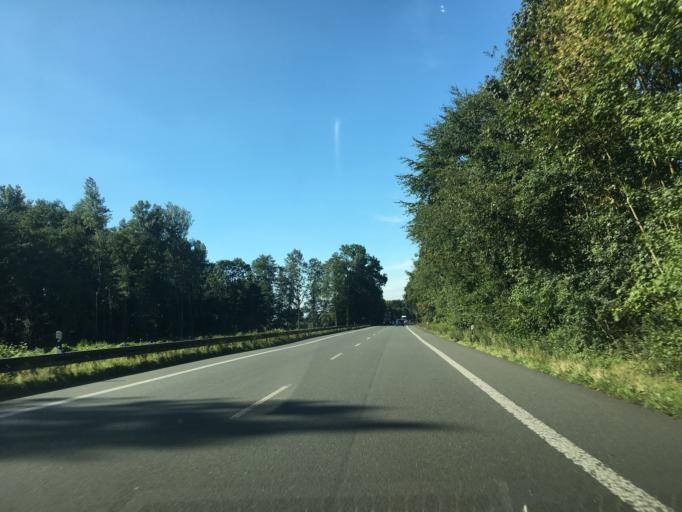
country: DE
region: North Rhine-Westphalia
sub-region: Regierungsbezirk Detmold
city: Rheda-Wiedenbruck
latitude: 51.8658
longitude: 8.3097
